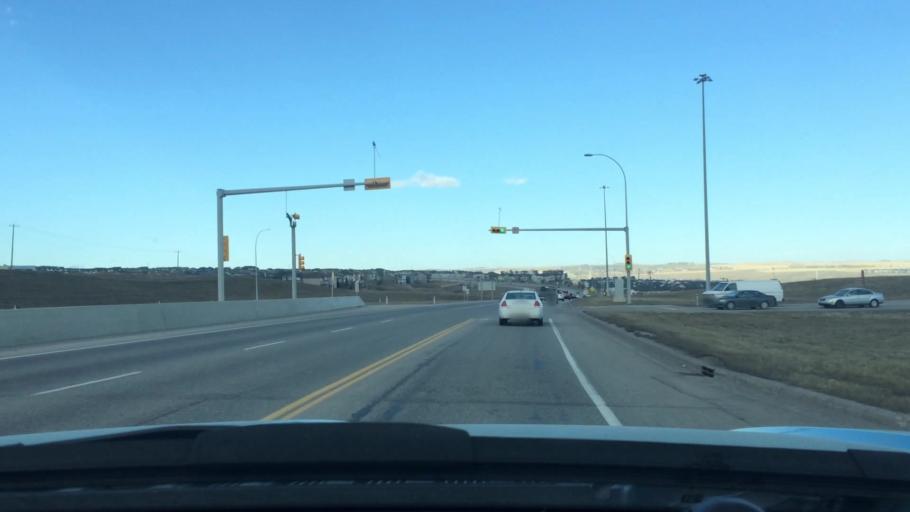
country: CA
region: Alberta
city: Calgary
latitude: 51.1536
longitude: -114.1409
